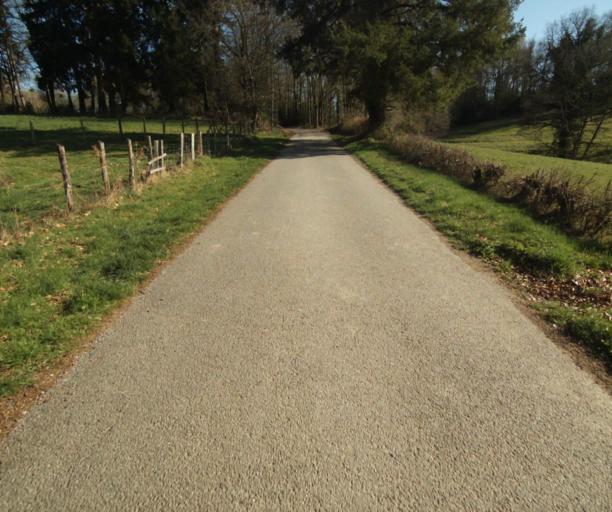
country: FR
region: Limousin
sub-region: Departement de la Correze
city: Chamboulive
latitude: 45.4745
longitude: 1.6970
